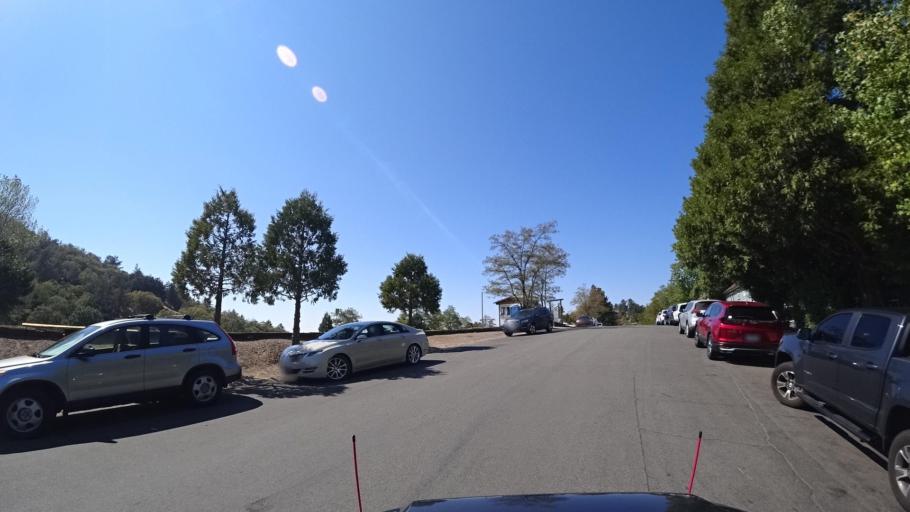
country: US
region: California
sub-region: San Diego County
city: Julian
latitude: 33.0768
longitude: -116.6013
